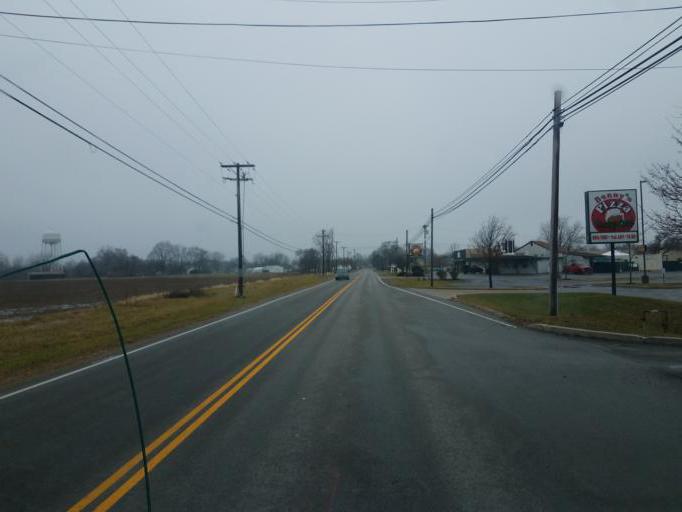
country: US
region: Ohio
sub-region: Union County
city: Marysville
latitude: 40.2324
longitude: -83.3520
